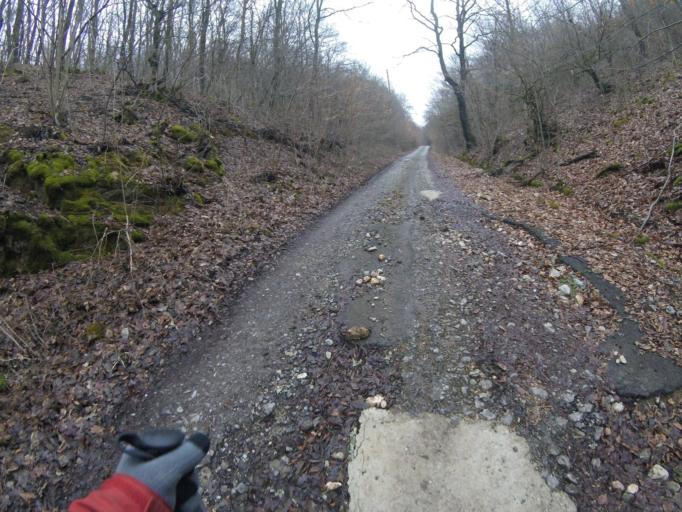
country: HU
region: Borsod-Abauj-Zemplen
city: Rudabanya
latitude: 48.4468
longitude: 20.5780
